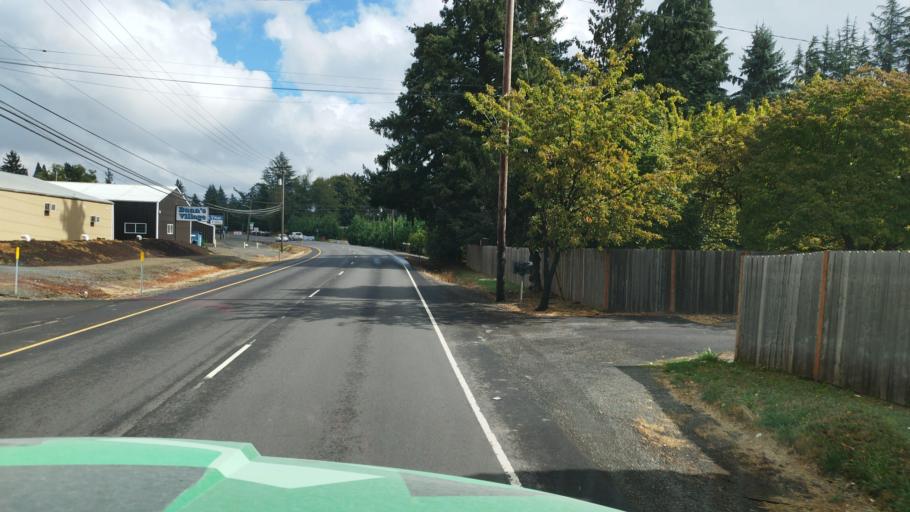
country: US
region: Oregon
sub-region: Yamhill County
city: Lafayette
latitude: 45.2337
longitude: -123.1543
